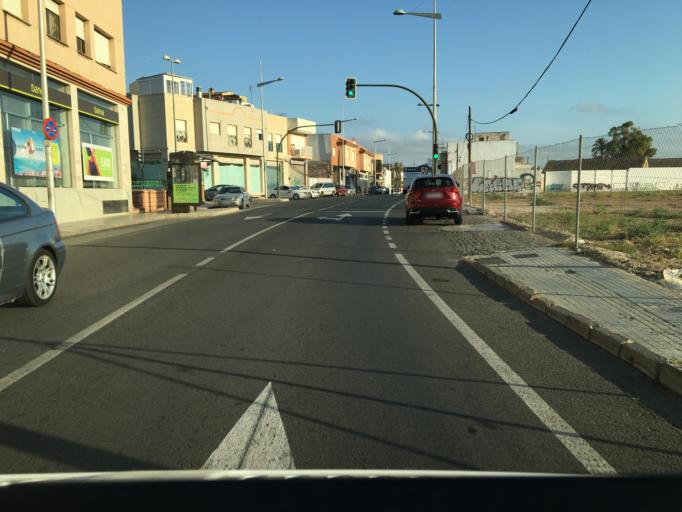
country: ES
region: Murcia
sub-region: Murcia
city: Cartagena
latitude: 37.6196
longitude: -0.9971
